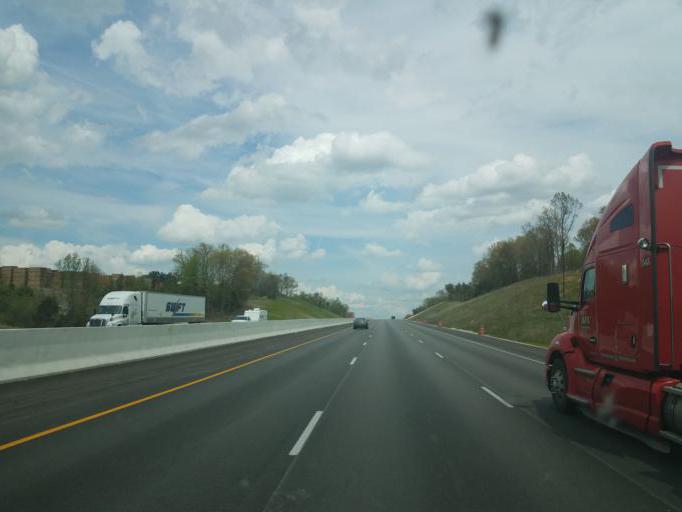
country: US
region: Kentucky
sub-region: Hart County
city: Munfordville
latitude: 37.3193
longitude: -85.9056
